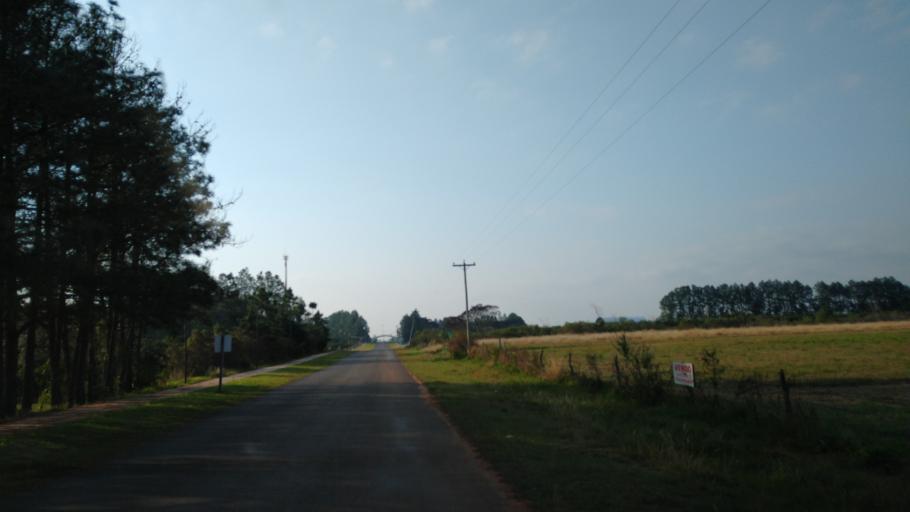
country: AR
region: Entre Rios
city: Santa Ana
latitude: -30.9041
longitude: -57.9250
